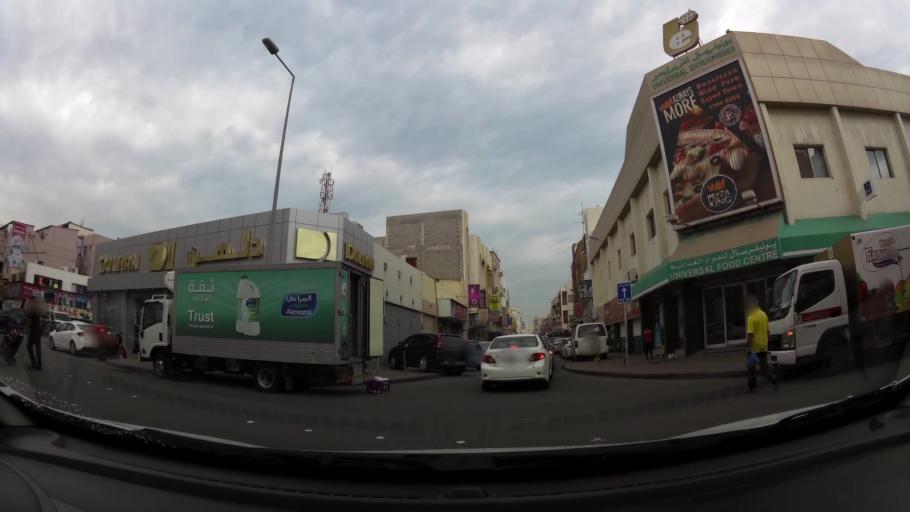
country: BH
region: Manama
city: Manama
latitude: 26.2272
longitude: 50.5923
